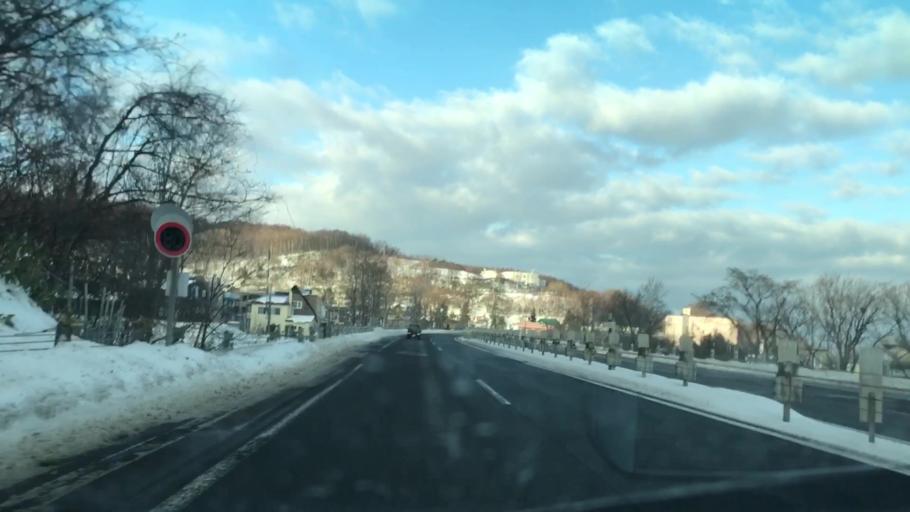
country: JP
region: Hokkaido
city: Otaru
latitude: 43.1406
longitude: 141.1491
